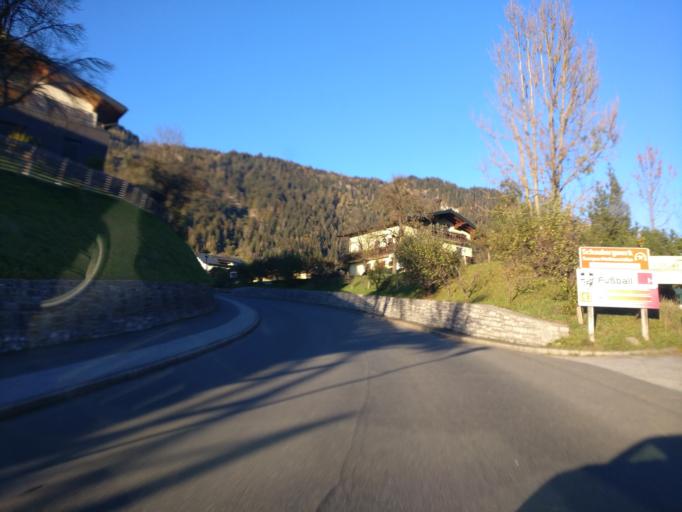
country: AT
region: Salzburg
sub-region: Politischer Bezirk Sankt Johann im Pongau
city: Sankt Veit im Pongau
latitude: 47.3274
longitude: 13.1534
